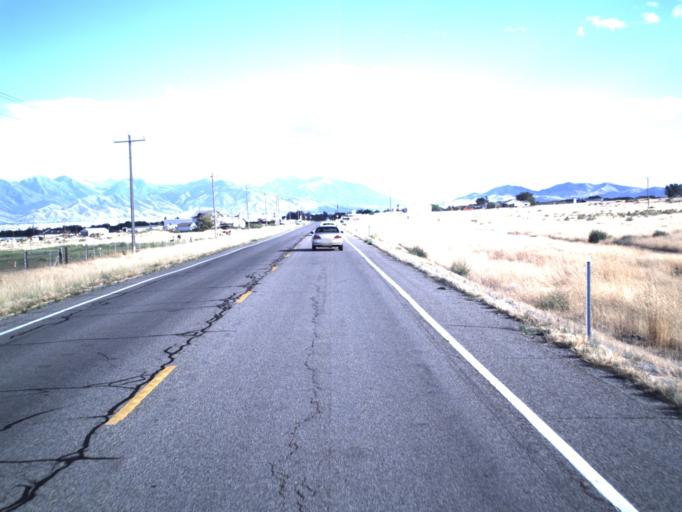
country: US
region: Utah
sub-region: Tooele County
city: Grantsville
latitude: 40.6096
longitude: -112.4920
